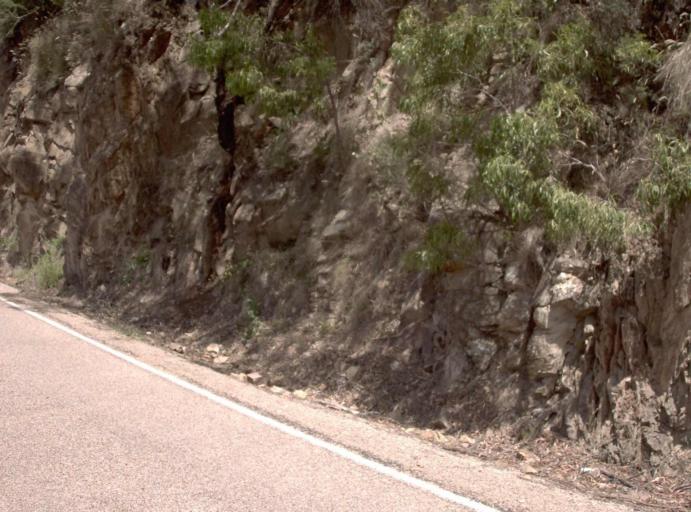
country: AU
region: Victoria
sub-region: East Gippsland
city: Lakes Entrance
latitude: -37.5484
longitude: 147.8667
